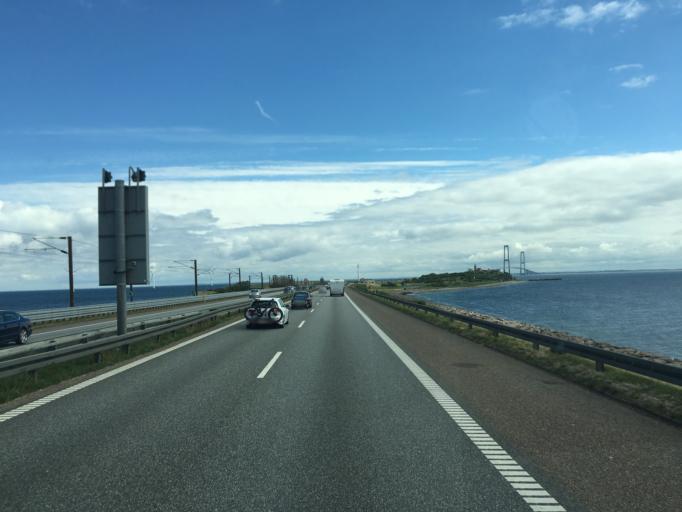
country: DK
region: South Denmark
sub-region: Nyborg Kommune
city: Nyborg
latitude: 55.3257
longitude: 10.9472
